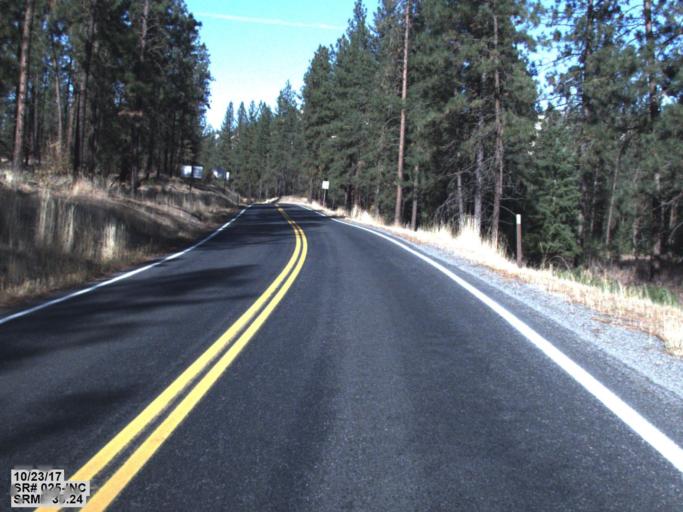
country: US
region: Washington
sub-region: Lincoln County
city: Davenport
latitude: 48.0732
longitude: -118.1970
